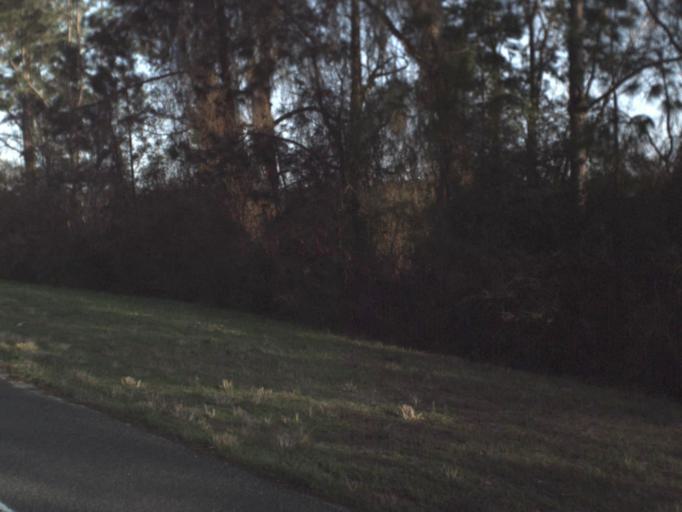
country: US
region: Florida
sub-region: Bay County
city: Lynn Haven
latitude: 30.4397
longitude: -85.7736
